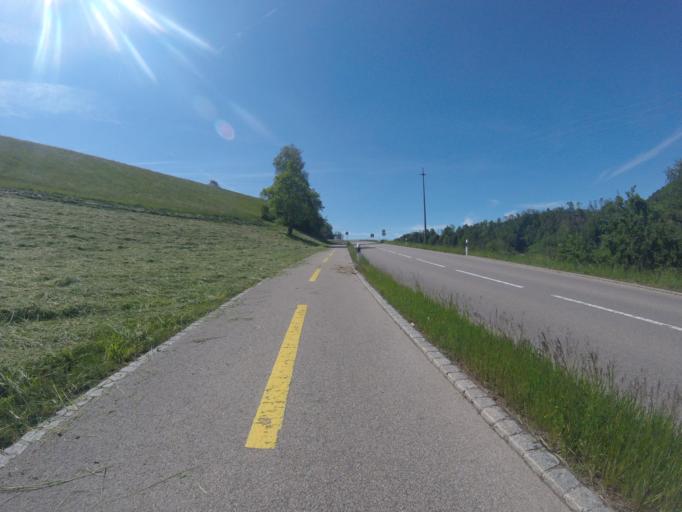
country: CH
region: Saint Gallen
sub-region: Wahlkreis Toggenburg
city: Ganterschwil
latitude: 47.3825
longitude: 9.0995
